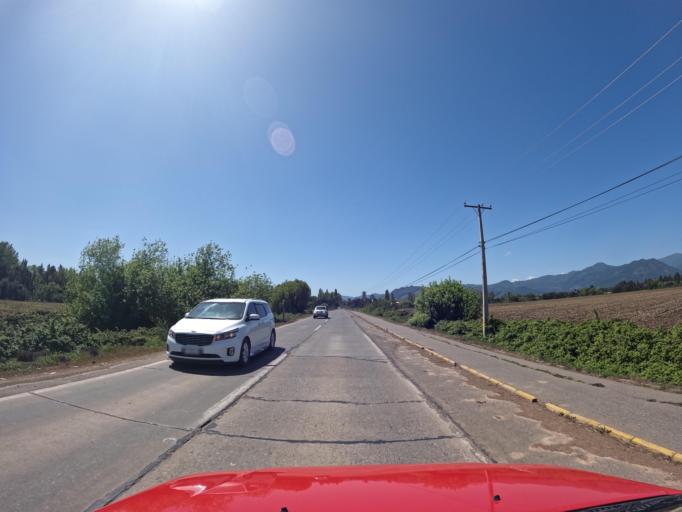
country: CL
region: Maule
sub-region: Provincia de Linares
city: Colbun
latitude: -35.7690
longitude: -71.4259
